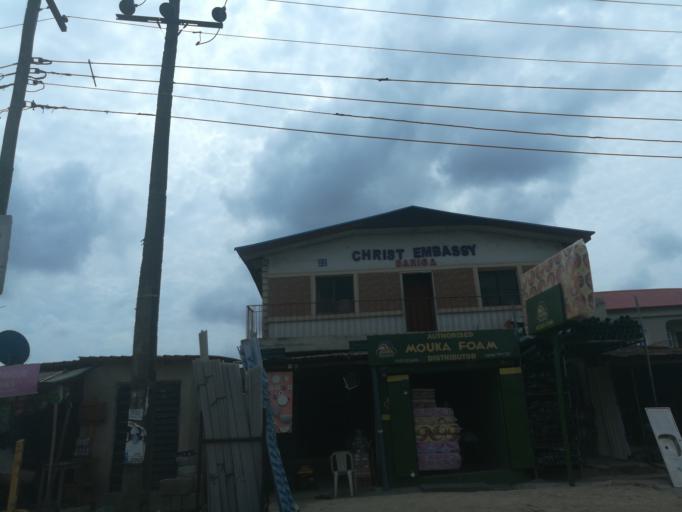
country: NG
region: Lagos
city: Somolu
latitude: 6.5456
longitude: 3.3941
